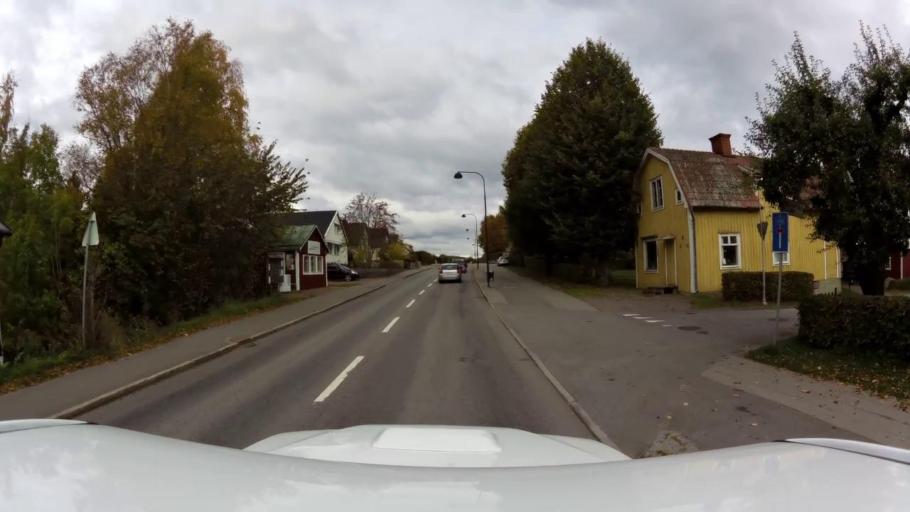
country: SE
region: OEstergoetland
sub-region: Linkopings Kommun
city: Berg
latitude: 58.4870
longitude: 15.5253
